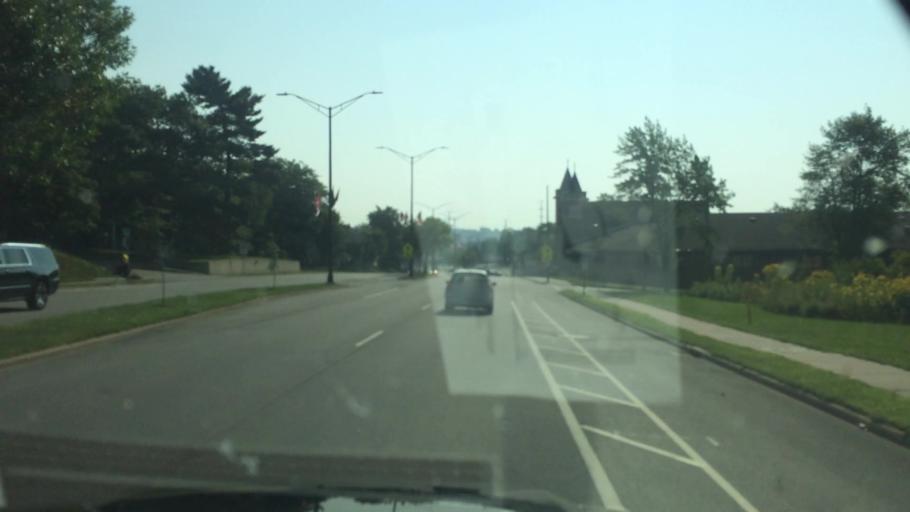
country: US
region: Wisconsin
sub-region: Marathon County
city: Wausau
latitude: 44.9592
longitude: -89.6439
